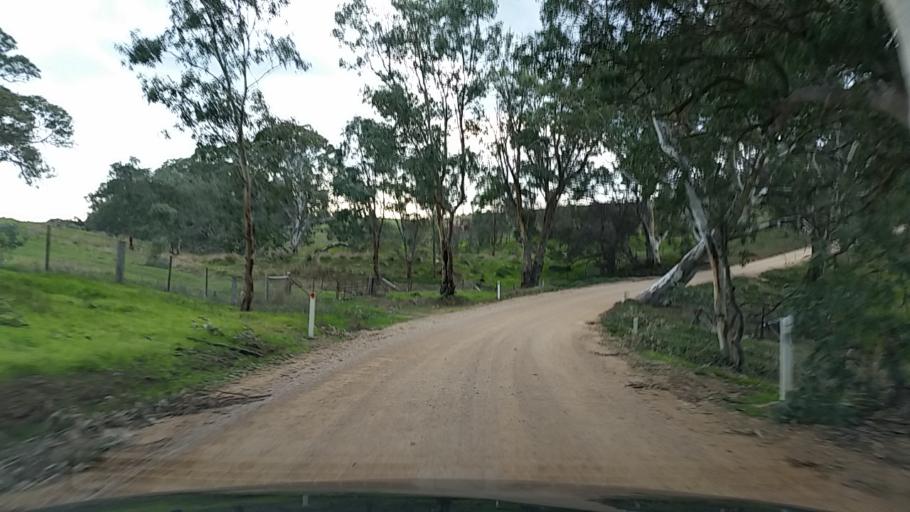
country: AU
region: South Australia
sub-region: Mount Barker
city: Nairne
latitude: -34.9662
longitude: 139.0243
